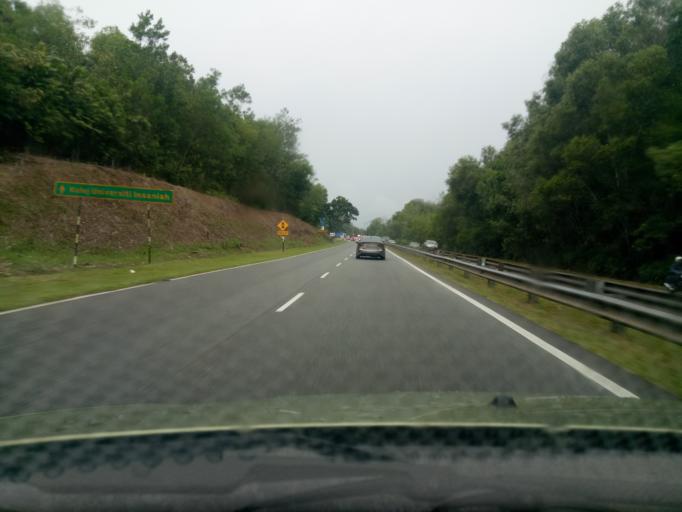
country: MY
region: Kedah
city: Sungai Petani
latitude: 5.6506
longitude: 100.5383
